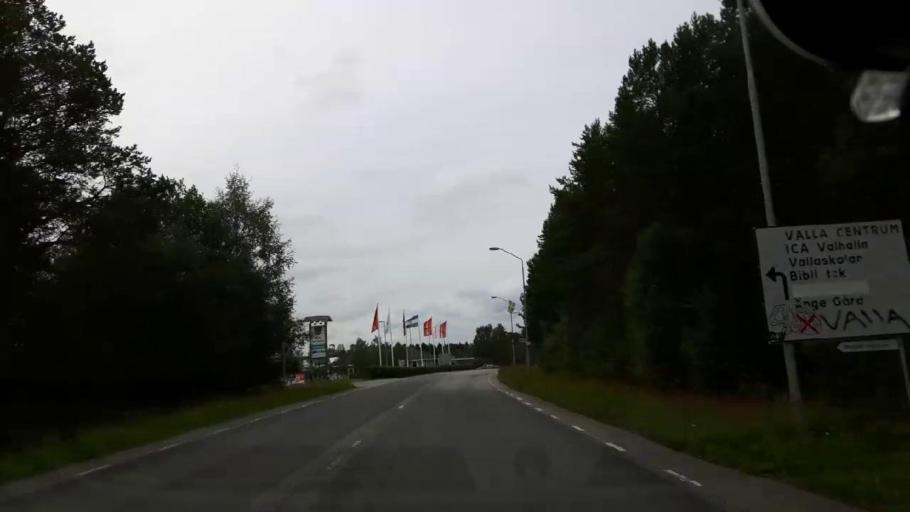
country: SE
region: Jaemtland
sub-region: OEstersunds Kommun
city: Ostersund
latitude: 63.1700
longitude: 14.5678
